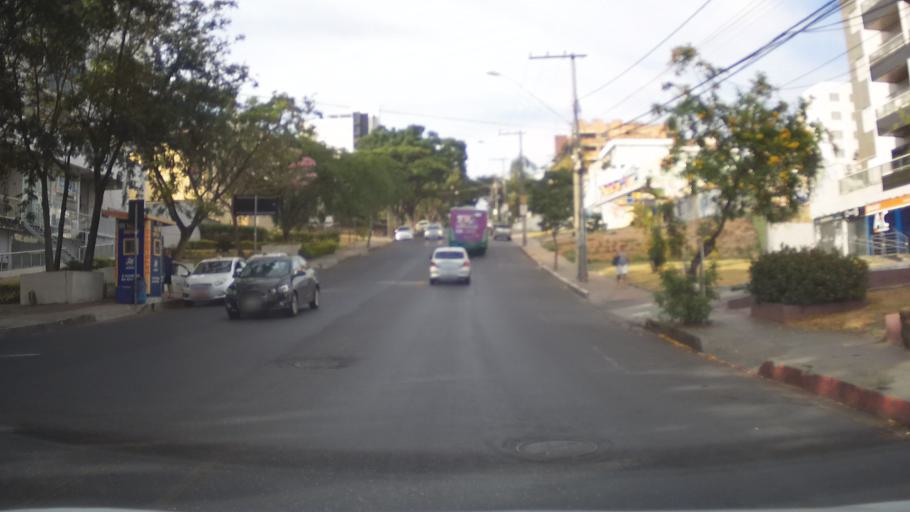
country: BR
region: Minas Gerais
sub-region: Belo Horizonte
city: Belo Horizonte
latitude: -19.8789
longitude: -43.9971
